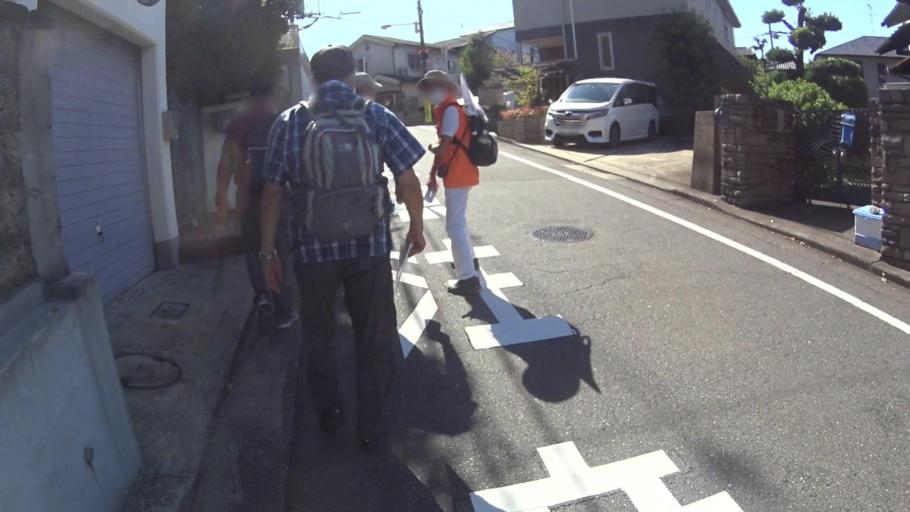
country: JP
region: Osaka
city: Takaishi
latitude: 34.5024
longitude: 135.4384
